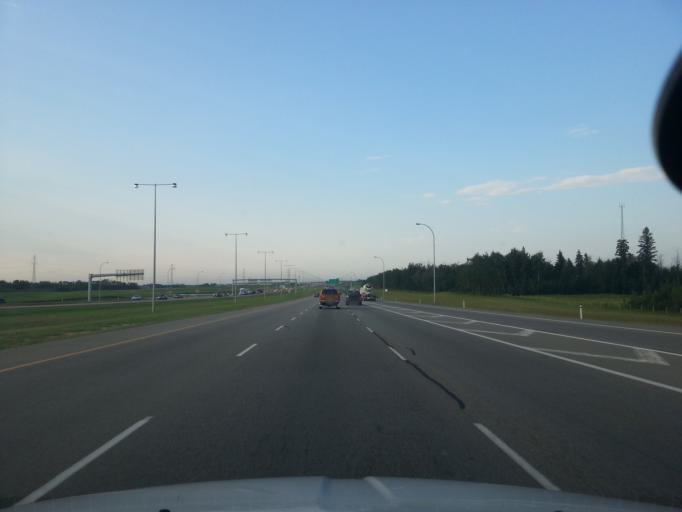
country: CA
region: Alberta
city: St. Albert
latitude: 53.5354
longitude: -113.6596
